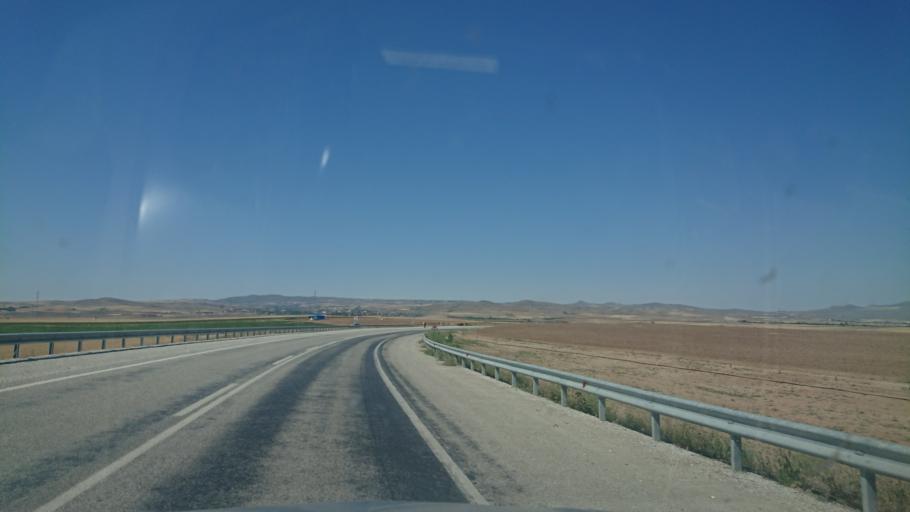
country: TR
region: Aksaray
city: Sariyahsi
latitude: 39.0211
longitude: 33.8827
